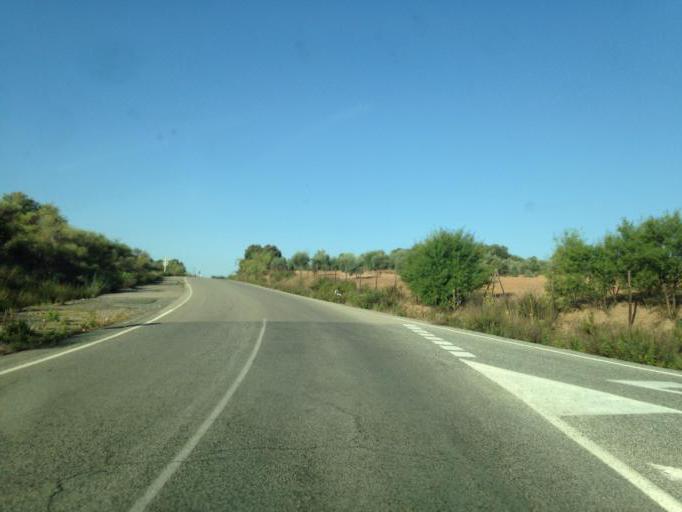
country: ES
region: Andalusia
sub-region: Provincia de Malaga
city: Villanueva de Tapia
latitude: 37.1312
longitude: -4.2862
